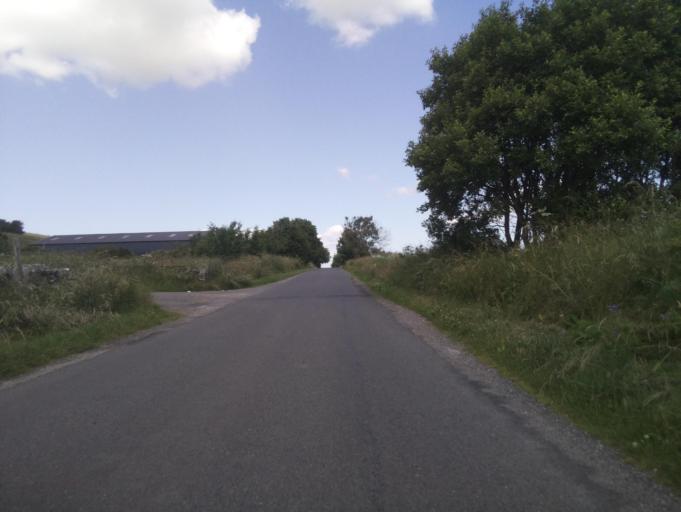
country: GB
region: England
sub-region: Derbyshire
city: Tideswell
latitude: 53.2305
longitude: -1.7864
